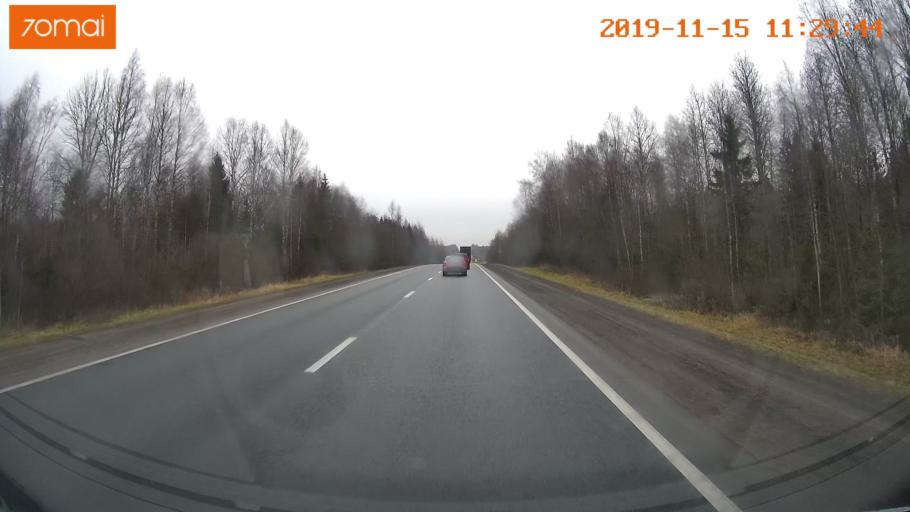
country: RU
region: Vologda
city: Molochnoye
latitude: 59.1767
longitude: 39.5165
